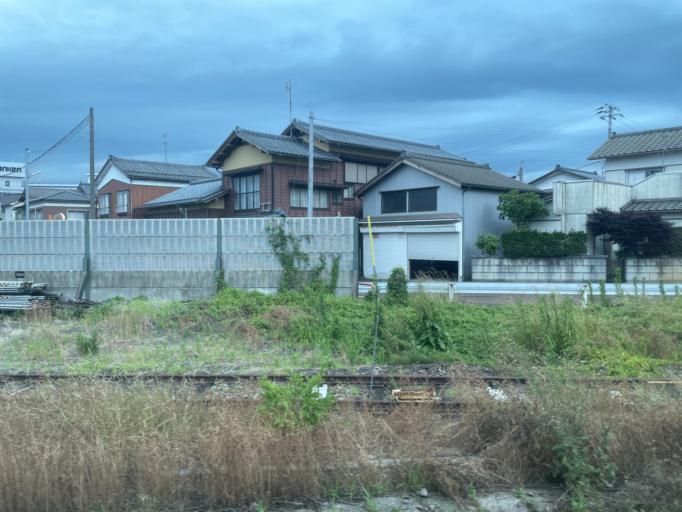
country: JP
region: Niigata
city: Yoshida-kasugacho
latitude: 37.6856
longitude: 138.8762
